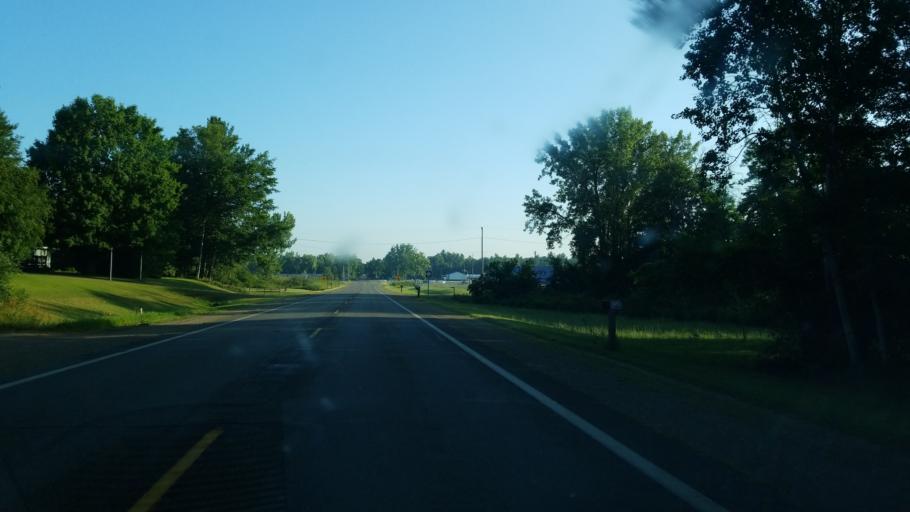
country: US
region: Michigan
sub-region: Montcalm County
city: Edmore
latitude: 43.4041
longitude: -85.0847
